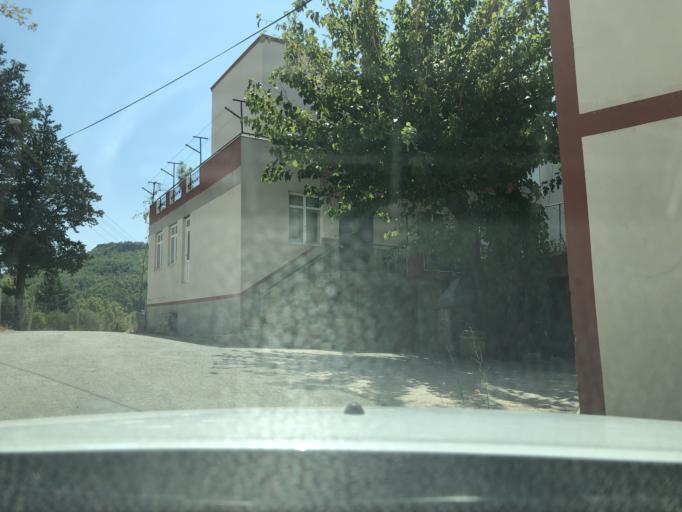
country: TR
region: Antalya
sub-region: Manavgat
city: Kizilagac
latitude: 36.8585
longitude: 31.5525
